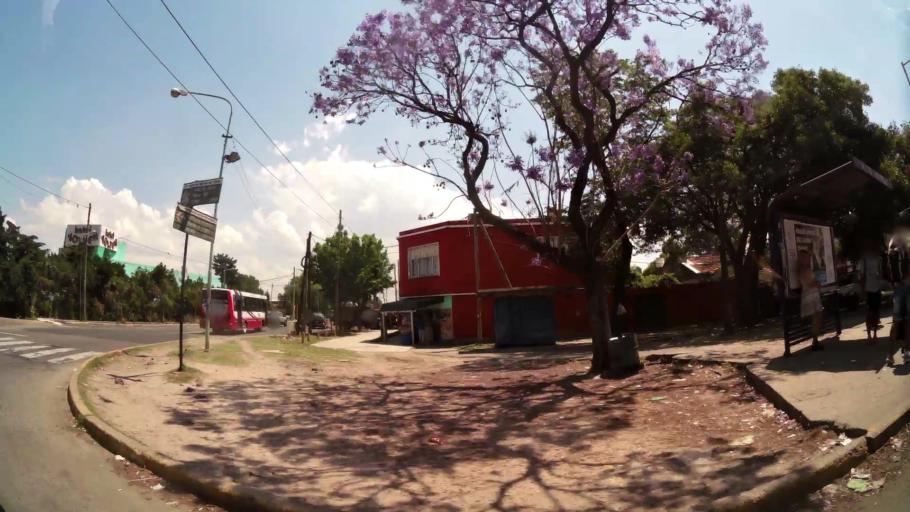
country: AR
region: Buenos Aires
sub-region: Partido de Tigre
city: Tigre
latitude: -34.4449
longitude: -58.5802
